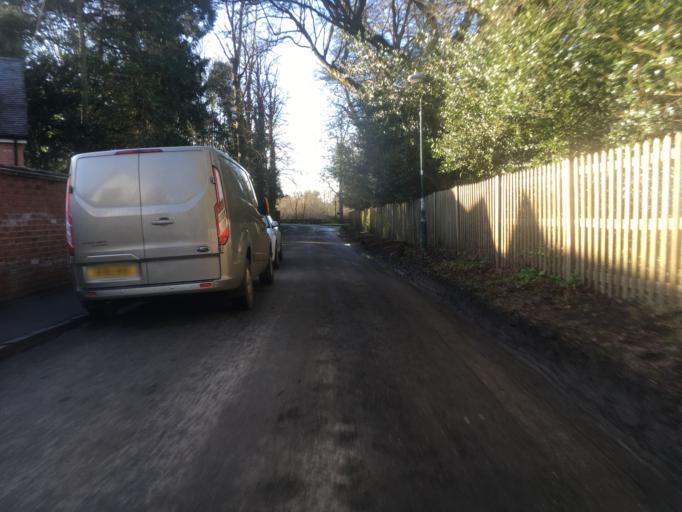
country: GB
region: England
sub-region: Warwickshire
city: Stratford-upon-Avon
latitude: 52.2076
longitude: -1.6611
